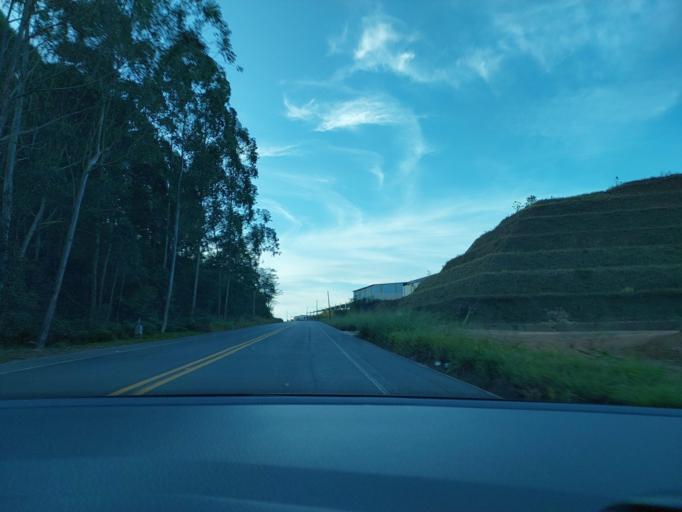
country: BR
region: Minas Gerais
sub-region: Vicosa
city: Vicosa
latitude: -20.8111
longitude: -42.8284
